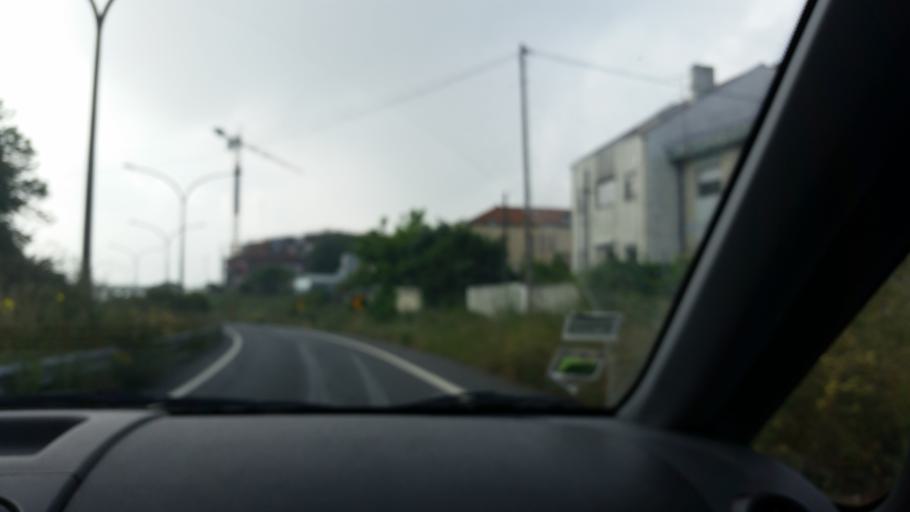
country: PT
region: Porto
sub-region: Vila Nova de Gaia
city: Canidelo
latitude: 41.1501
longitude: -8.6442
